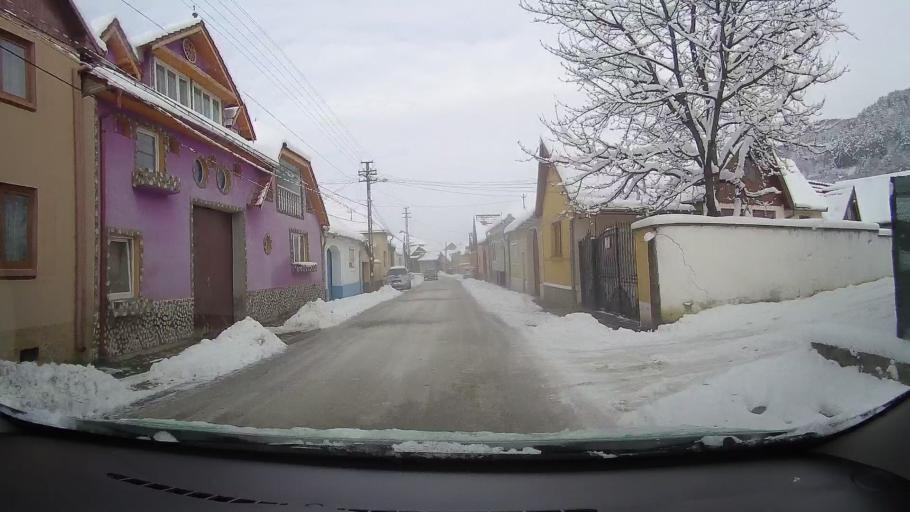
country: RO
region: Alba
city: Pianu de Sus
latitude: 45.8937
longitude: 23.4835
